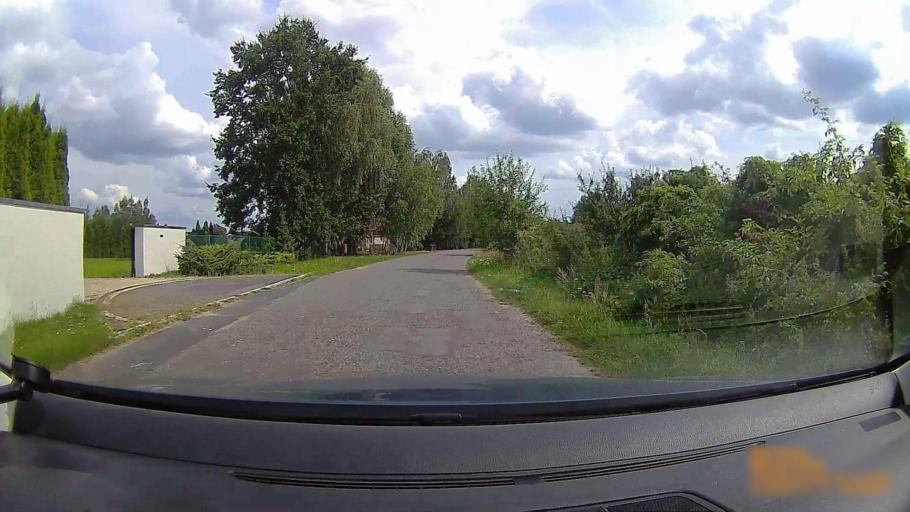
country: PL
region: Greater Poland Voivodeship
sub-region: Powiat koninski
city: Rychwal
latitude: 52.0808
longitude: 18.1564
